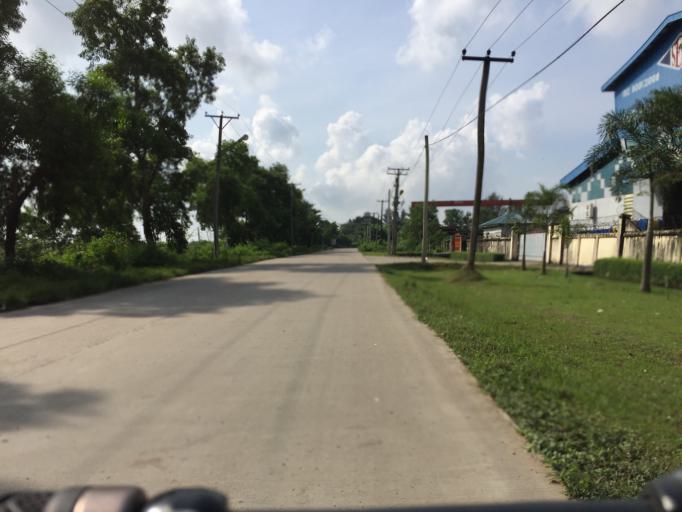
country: MM
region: Yangon
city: Syriam
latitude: 16.8296
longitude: 96.2223
